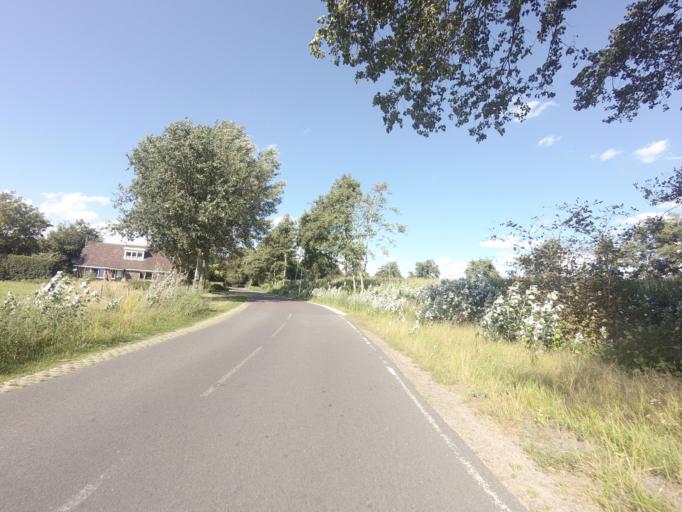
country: NL
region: Drenthe
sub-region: Gemeente Hoogeveen
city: Hoogeveen
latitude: 52.6099
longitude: 6.4678
